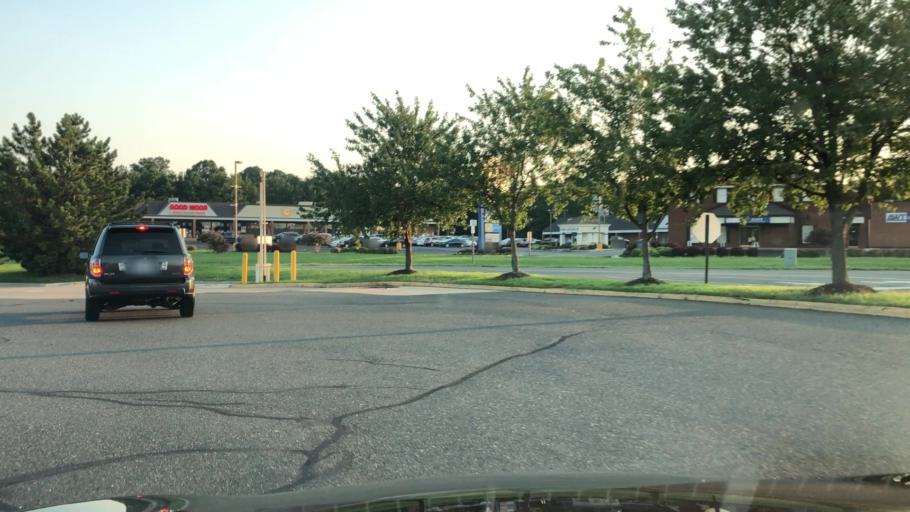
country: US
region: Virginia
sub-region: City of Fredericksburg
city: Fredericksburg
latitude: 38.2924
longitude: -77.5171
